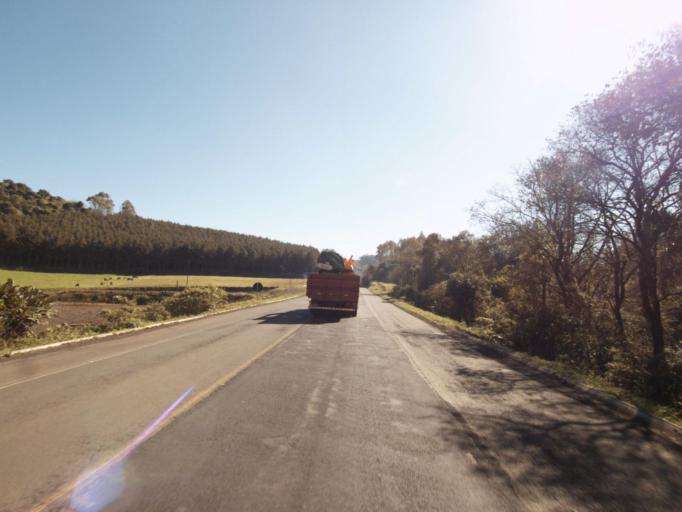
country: BR
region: Rio Grande do Sul
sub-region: Frederico Westphalen
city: Frederico Westphalen
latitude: -27.0537
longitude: -53.2287
